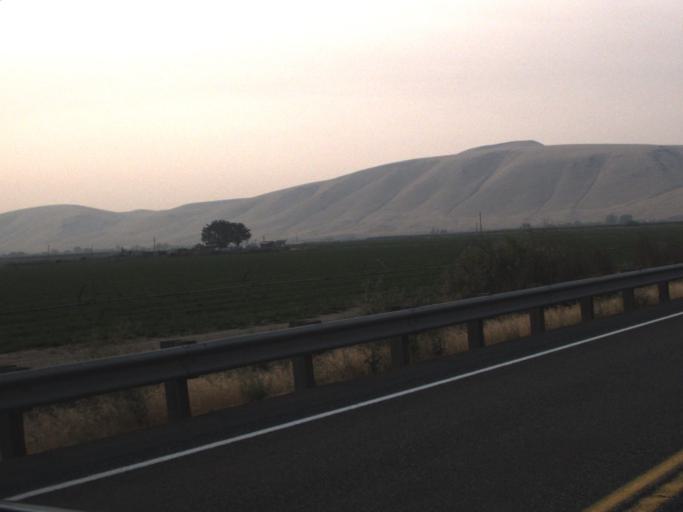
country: US
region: Washington
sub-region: Yakima County
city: Toppenish
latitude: 46.3301
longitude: -120.3205
